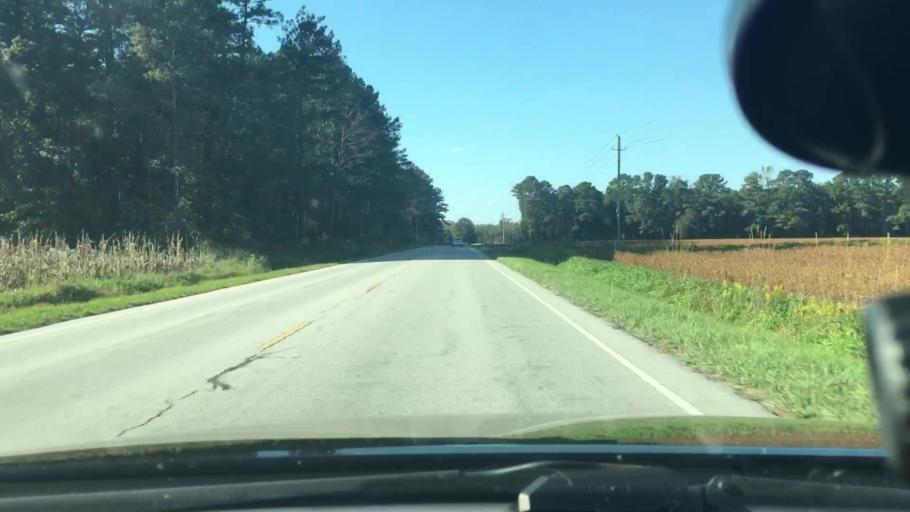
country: US
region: North Carolina
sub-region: Pitt County
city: Windsor
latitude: 35.4807
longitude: -77.2992
